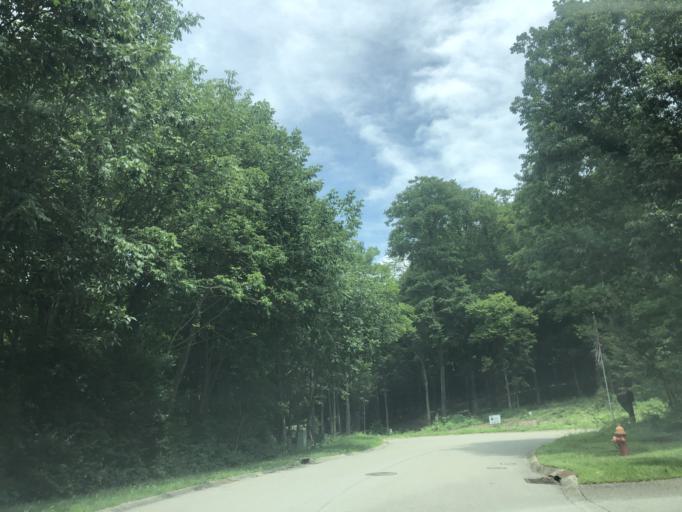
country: US
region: Tennessee
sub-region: Davidson County
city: Forest Hills
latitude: 36.0781
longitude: -86.8273
